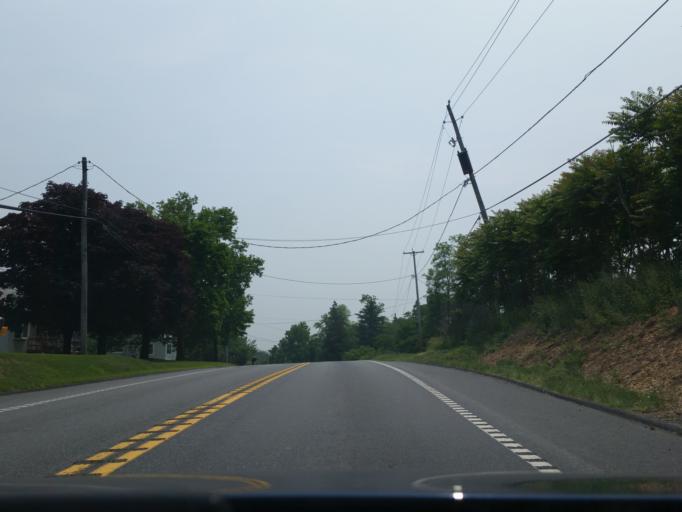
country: US
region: Pennsylvania
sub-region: Lebanon County
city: Jonestown
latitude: 40.4349
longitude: -76.5076
